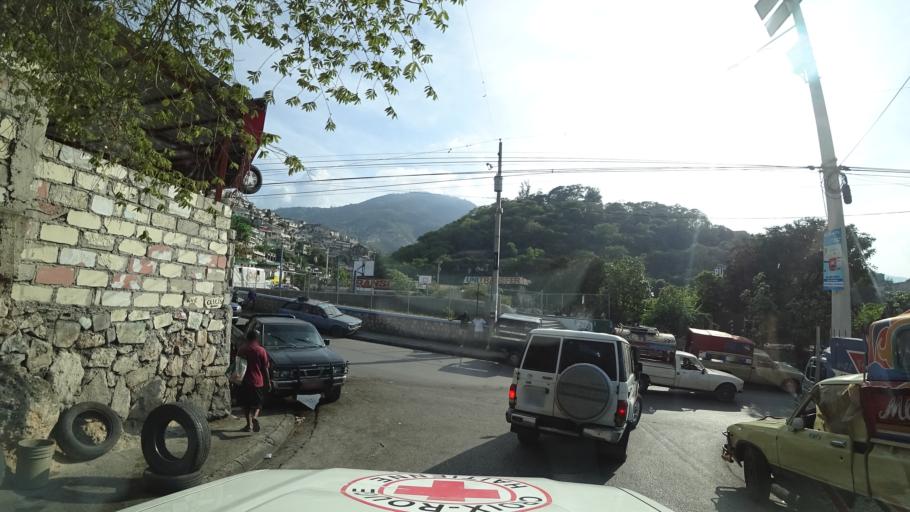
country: HT
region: Ouest
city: Delmas 73
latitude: 18.5329
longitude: -72.3159
